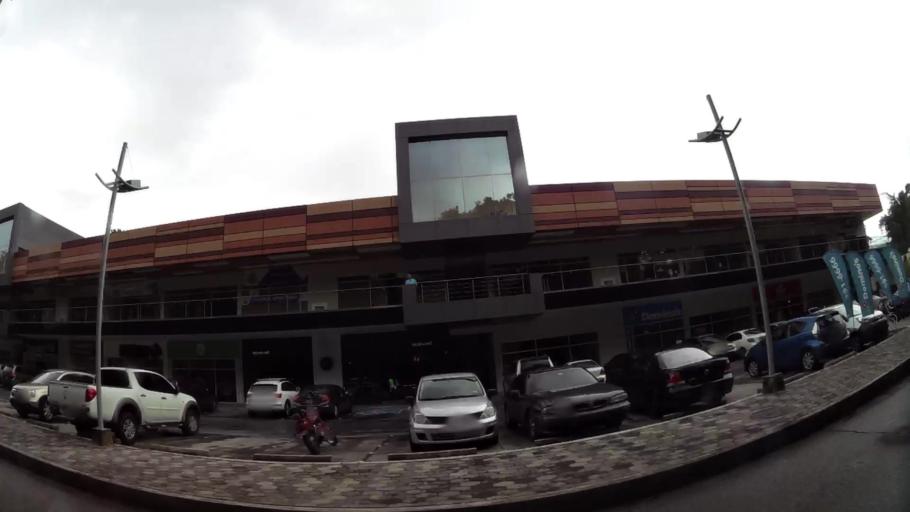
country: PA
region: Panama
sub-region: Distrito de Panama
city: Ancon
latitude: 9.0035
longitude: -79.5735
